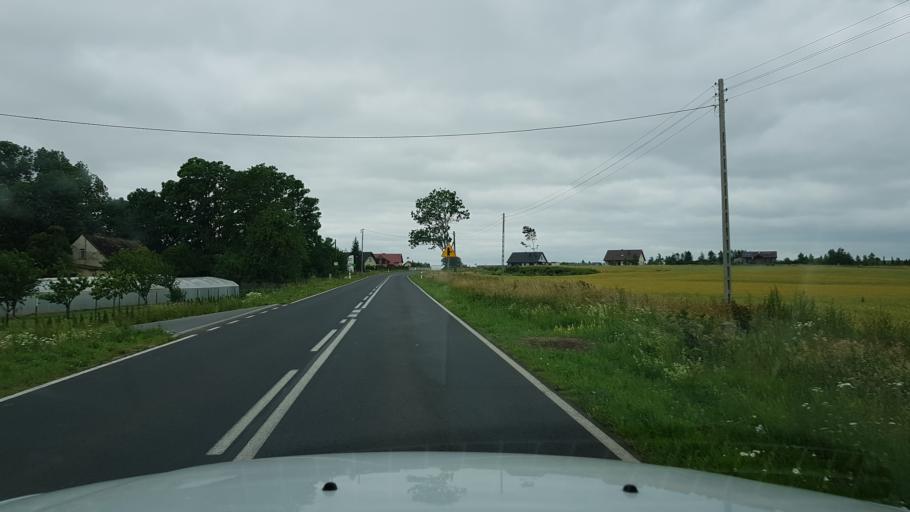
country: PL
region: West Pomeranian Voivodeship
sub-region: Powiat gryficki
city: Gryfice
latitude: 53.9062
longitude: 15.1798
